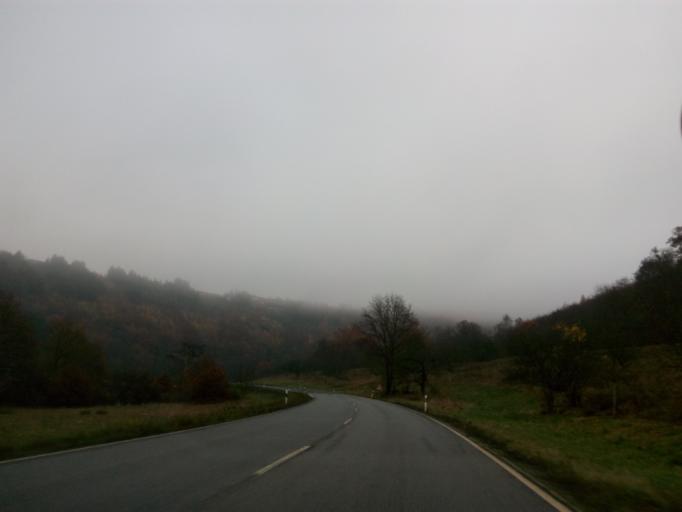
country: DE
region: Rheinland-Pfalz
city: Lohnweiler
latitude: 49.6209
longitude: 7.6137
